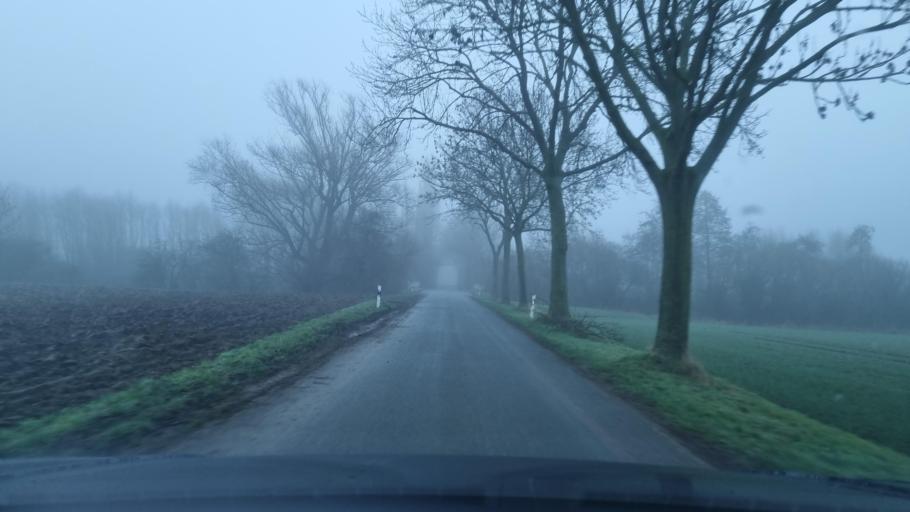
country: DE
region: North Rhine-Westphalia
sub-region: Regierungsbezirk Dusseldorf
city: Emmerich
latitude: 51.7998
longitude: 6.2403
